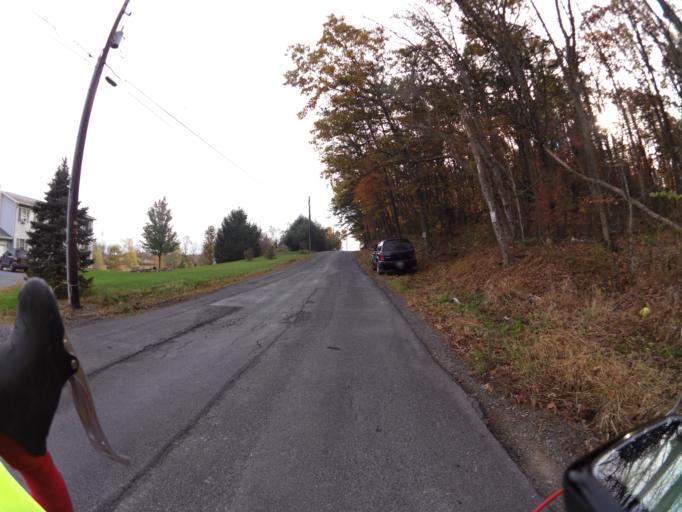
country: US
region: Pennsylvania
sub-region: Union County
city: New Columbia
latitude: 41.0280
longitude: -76.9316
